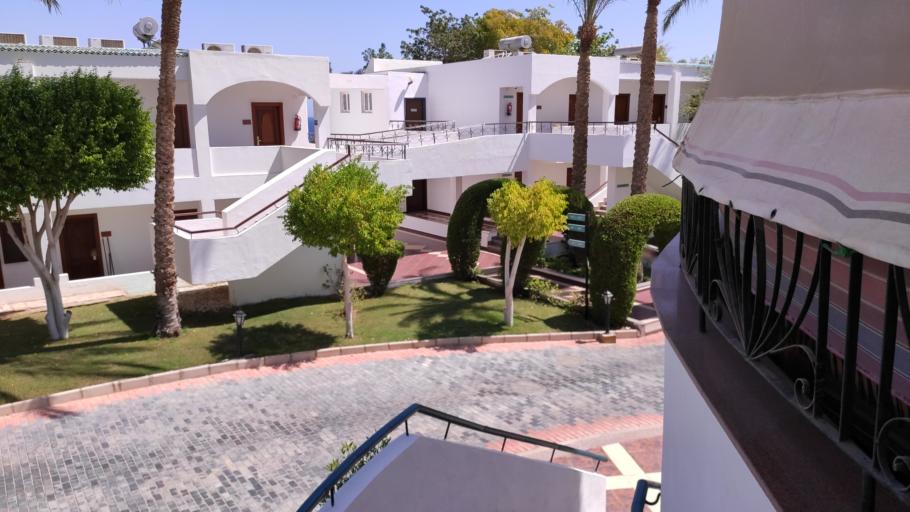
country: EG
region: South Sinai
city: Sharm el-Sheikh
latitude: 27.9446
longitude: 34.3826
